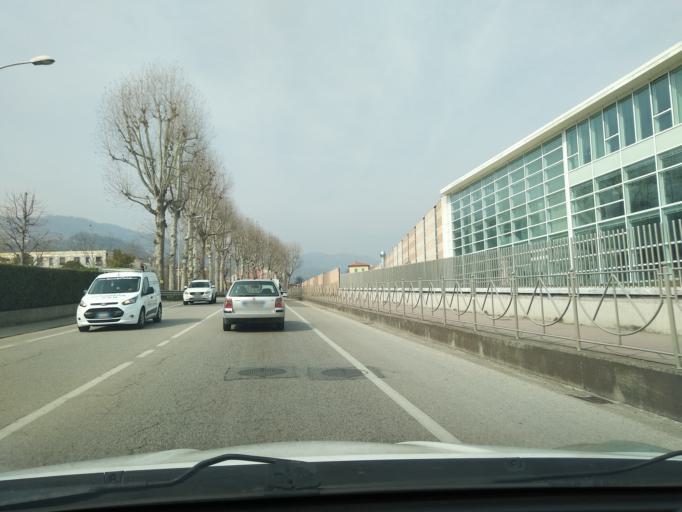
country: IT
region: Veneto
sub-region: Provincia di Vicenza
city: Chiampo
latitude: 45.5409
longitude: 11.2880
